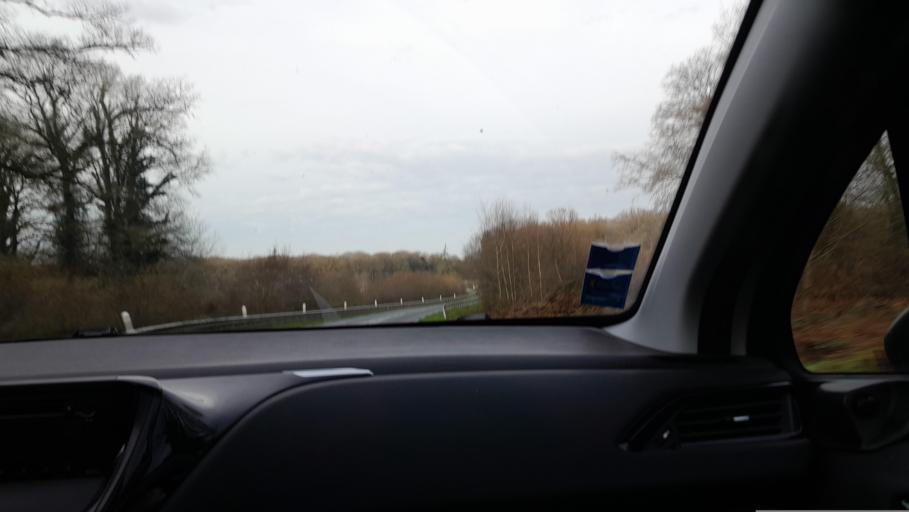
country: FR
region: Brittany
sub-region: Departement d'Ille-et-Vilaine
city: La Guerche-de-Bretagne
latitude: 47.9013
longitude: -1.1828
